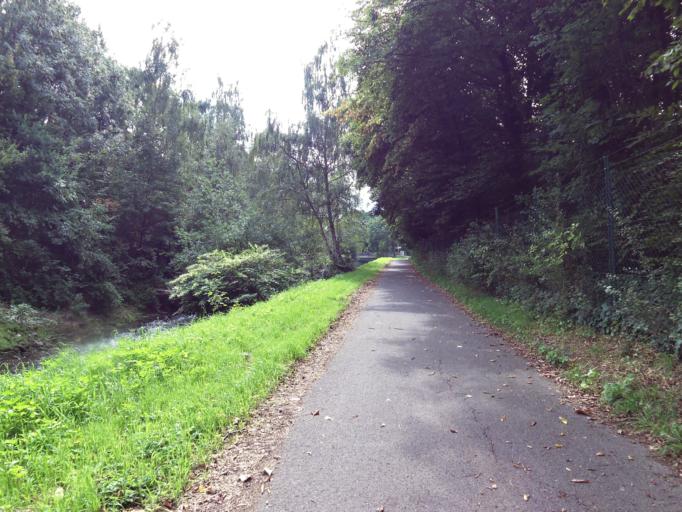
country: DE
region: North Rhine-Westphalia
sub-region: Regierungsbezirk Koln
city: Ubach-Palenberg
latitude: 50.9471
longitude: 6.1038
